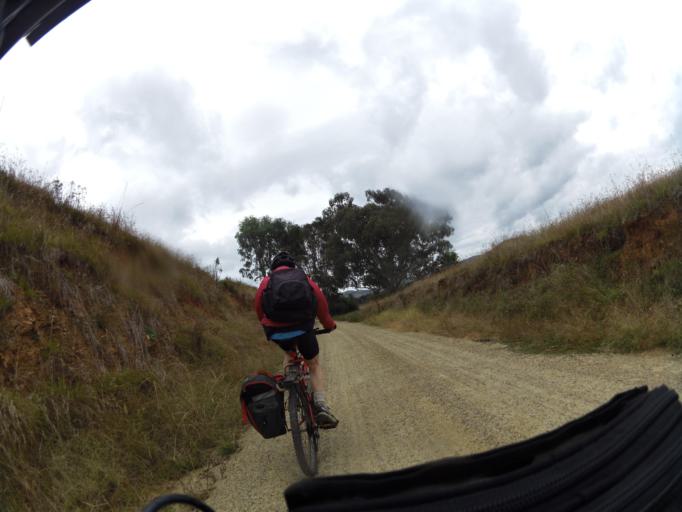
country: AU
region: New South Wales
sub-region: Albury Municipality
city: East Albury
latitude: -36.1918
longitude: 147.2995
